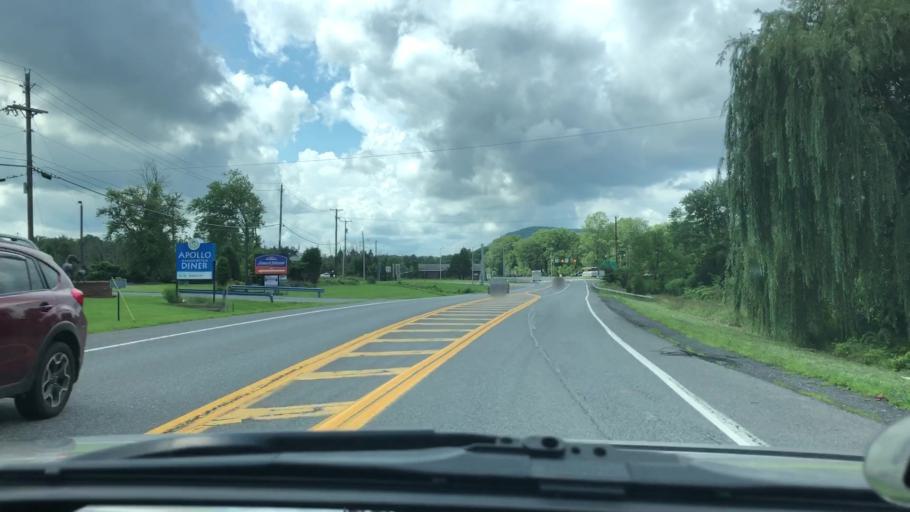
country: US
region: New York
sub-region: Ulster County
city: Saugerties
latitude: 42.0877
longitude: -73.9740
